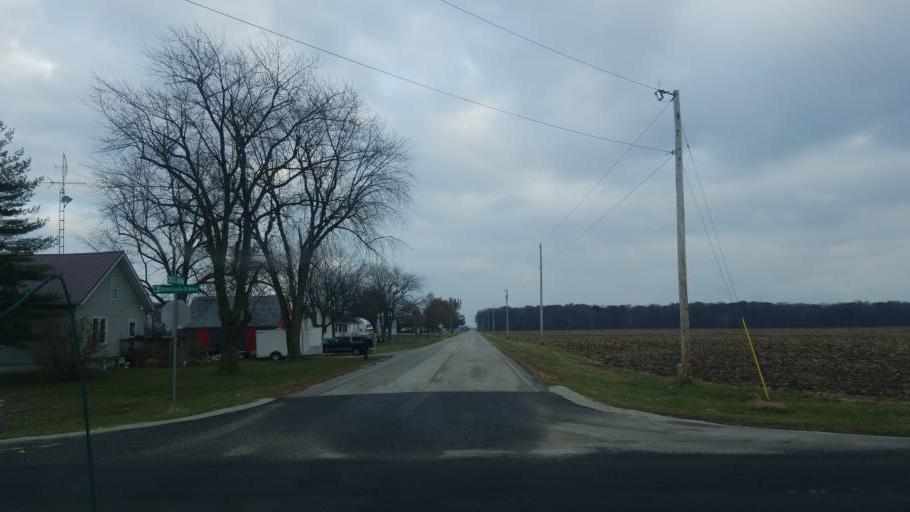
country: US
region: Ohio
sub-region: Mercer County
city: Coldwater
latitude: 40.5089
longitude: -84.6478
